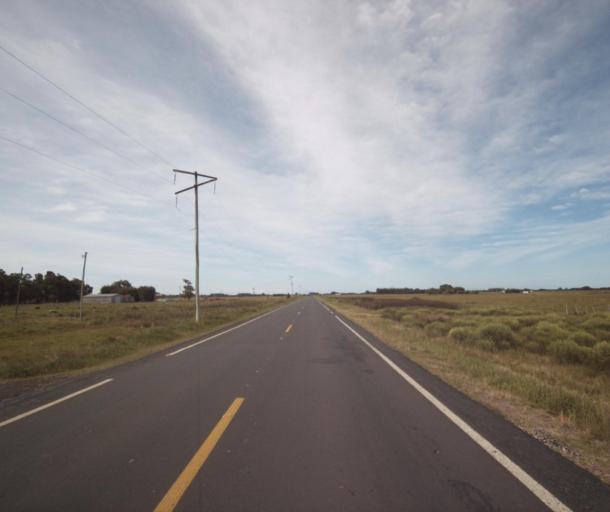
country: BR
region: Rio Grande do Sul
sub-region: Rio Grande
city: Rio Grande
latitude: -31.9370
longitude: -51.9681
